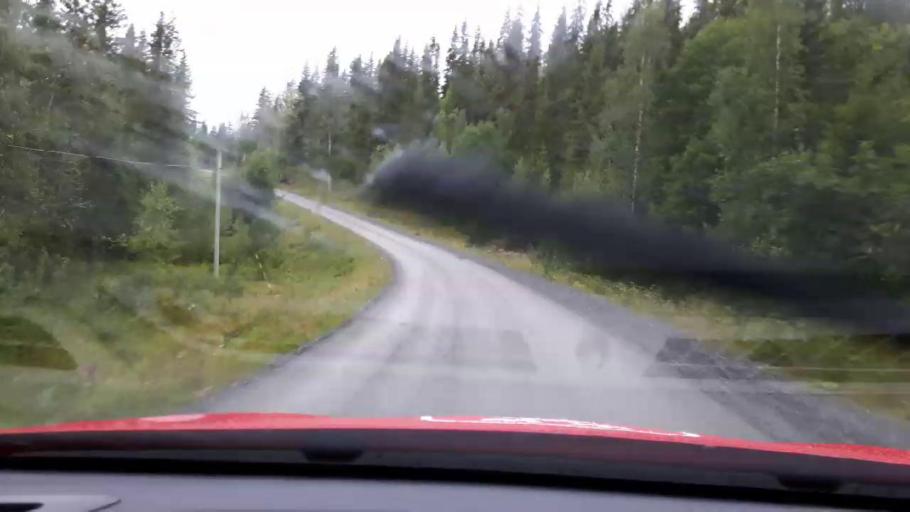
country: SE
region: Jaemtland
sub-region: Are Kommun
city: Are
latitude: 63.5066
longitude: 12.7371
